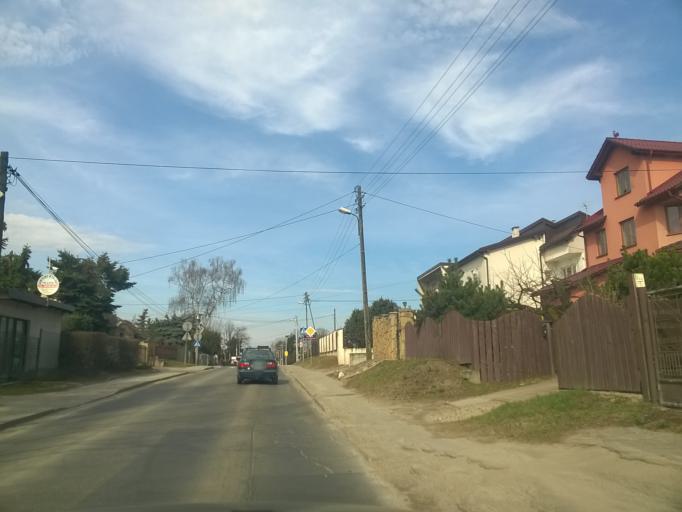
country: PL
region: Lesser Poland Voivodeship
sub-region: Powiat krakowski
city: Rzaska
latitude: 50.0821
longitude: 19.8551
